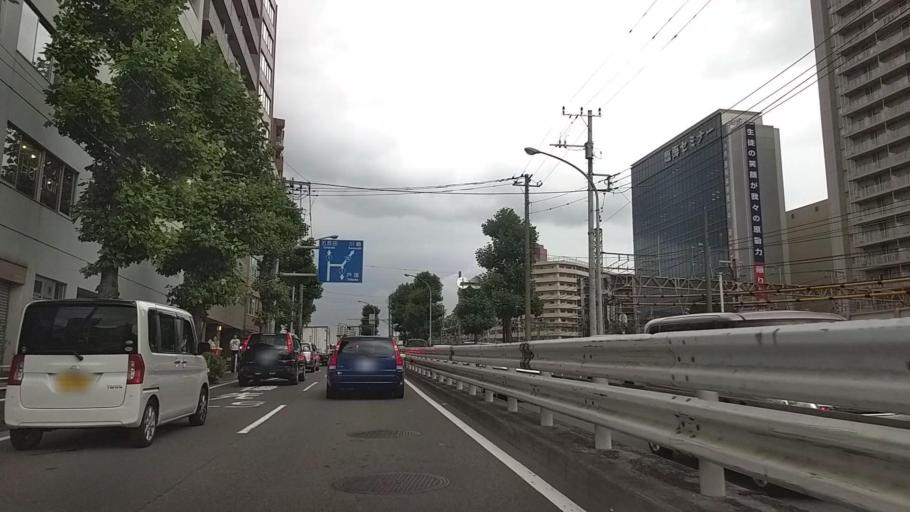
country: JP
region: Kanagawa
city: Yokohama
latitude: 35.4697
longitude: 139.6253
